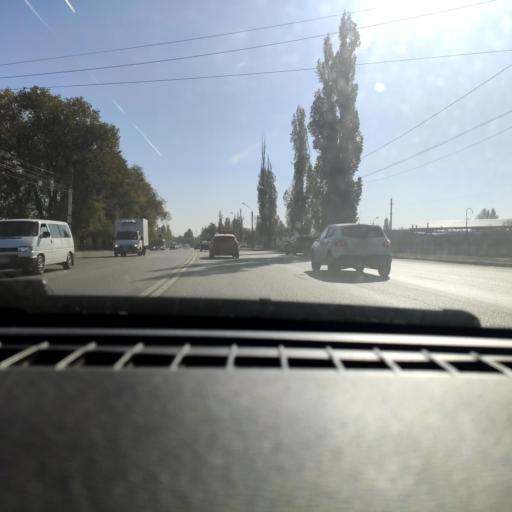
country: RU
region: Voronezj
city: Voronezh
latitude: 51.6285
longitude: 39.2301
